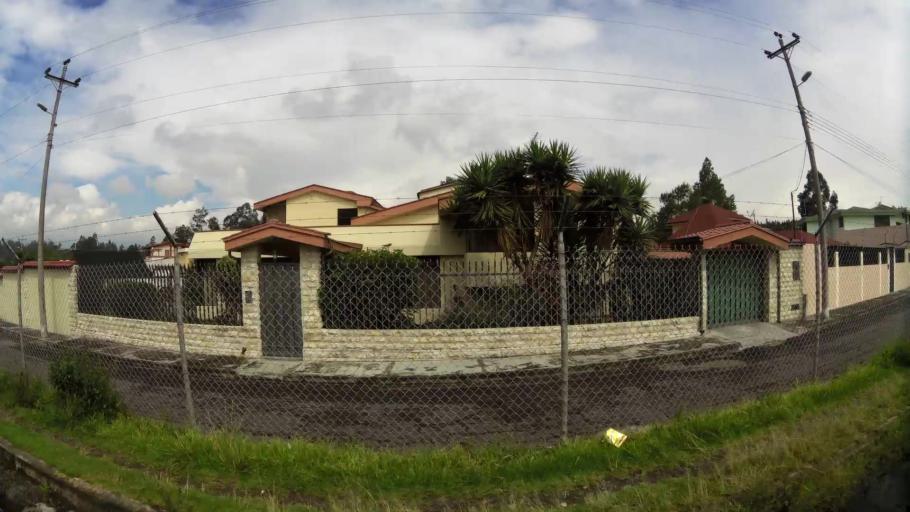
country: EC
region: Pichincha
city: Sangolqui
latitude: -0.3043
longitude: -78.4352
